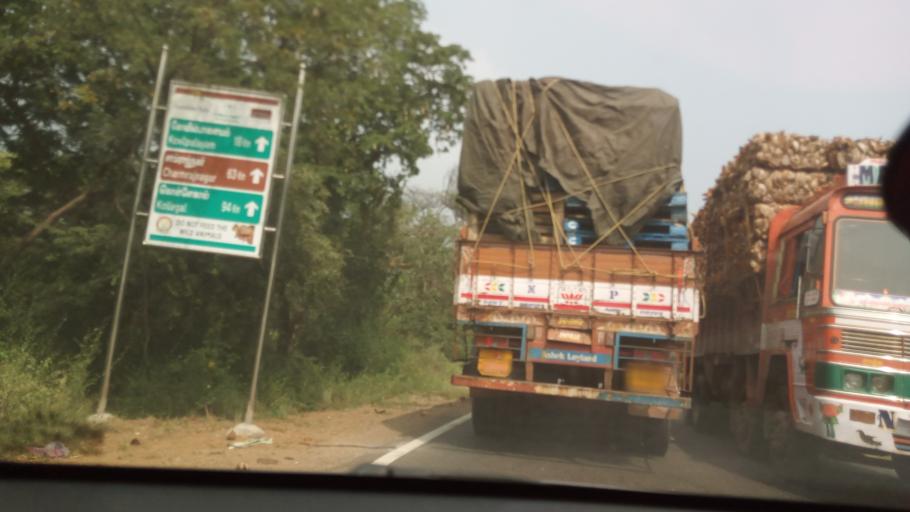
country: IN
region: Tamil Nadu
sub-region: Erode
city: Sathyamangalam
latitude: 11.5748
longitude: 77.1336
